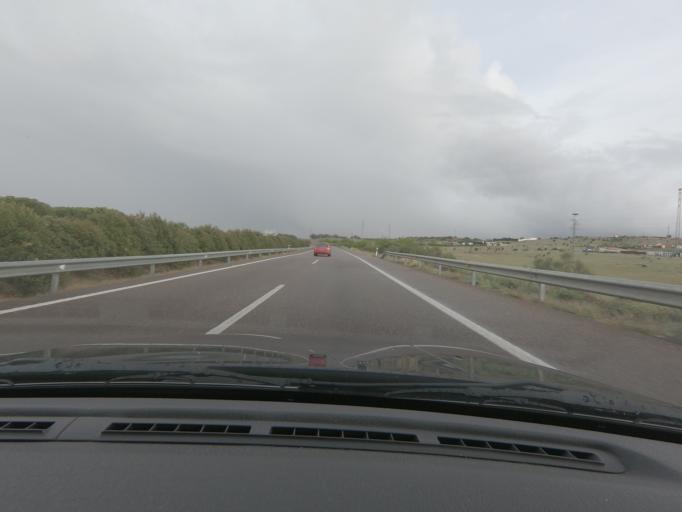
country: ES
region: Extremadura
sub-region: Provincia de Badajoz
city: Badajoz
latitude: 38.8790
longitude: -6.8854
